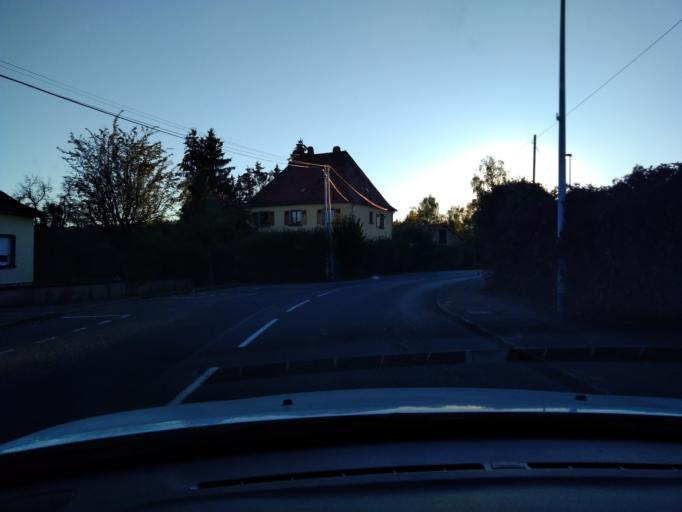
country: FR
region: Lorraine
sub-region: Departement de la Moselle
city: Sarreguemines
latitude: 49.1018
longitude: 7.0562
